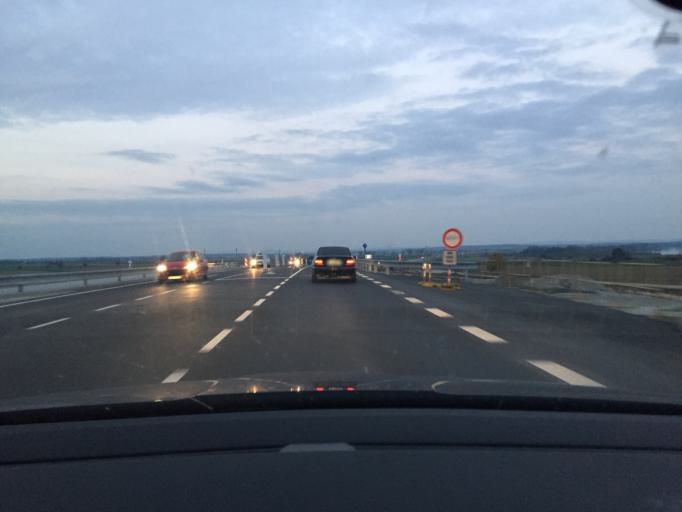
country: CZ
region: Jihocesky
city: Dolni Bukovsko
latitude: 49.1542
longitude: 14.6330
